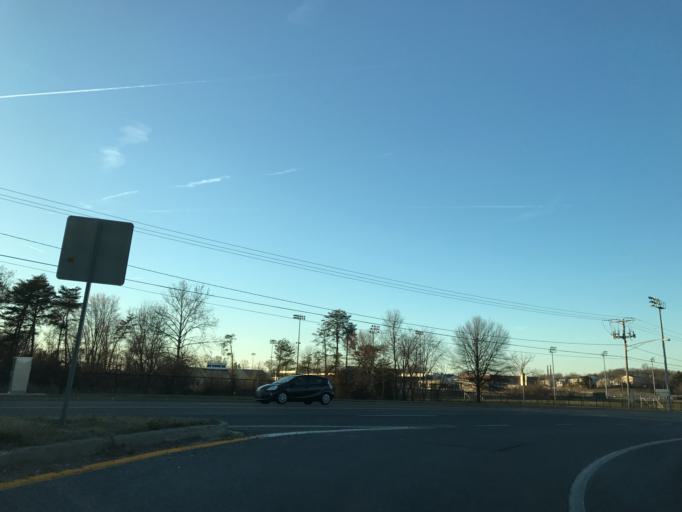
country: US
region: Maryland
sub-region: Anne Arundel County
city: Green Haven
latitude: 39.1409
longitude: -76.5263
